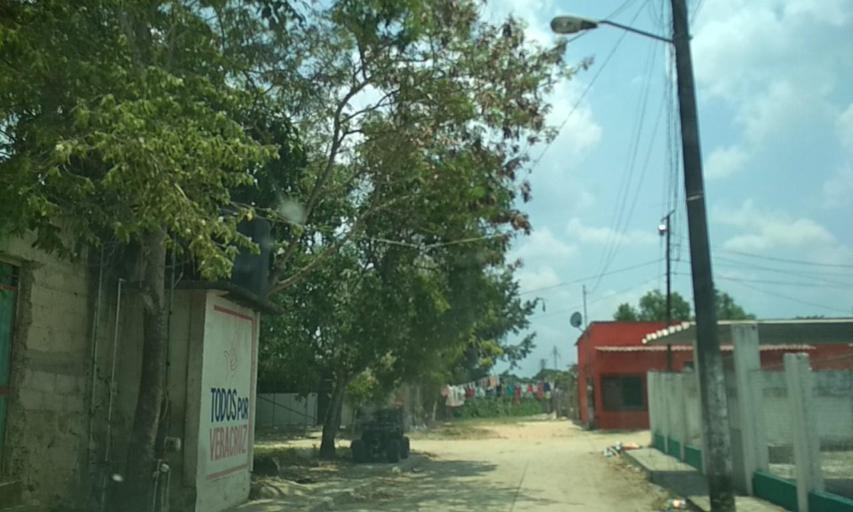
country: MX
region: Veracruz
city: Las Choapas
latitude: 17.9138
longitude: -94.0890
